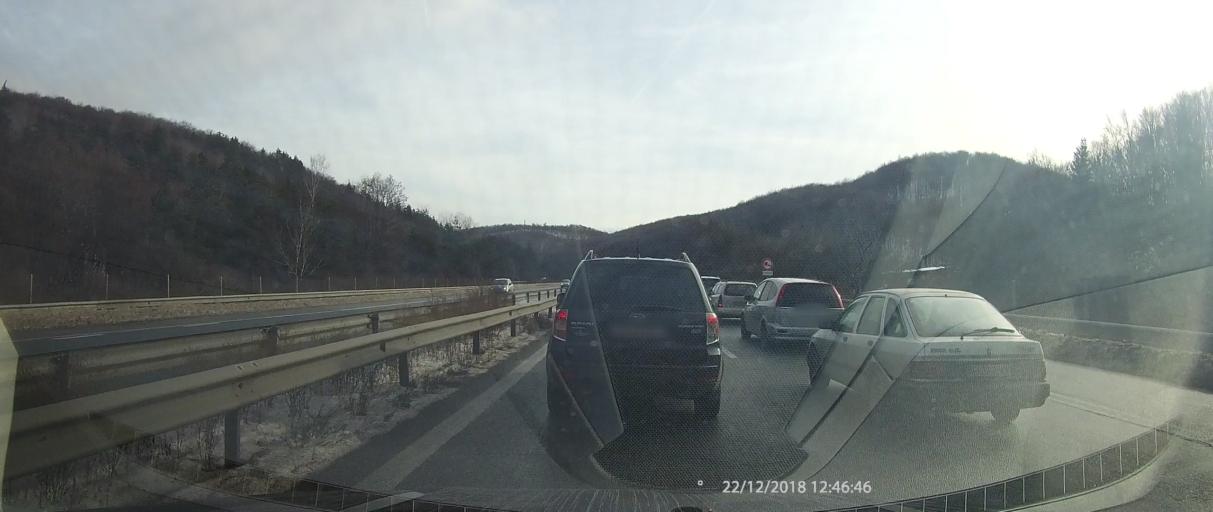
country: BG
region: Sofiya
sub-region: Obshtina Gorna Malina
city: Gorna Malina
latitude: 42.7770
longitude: 23.7746
